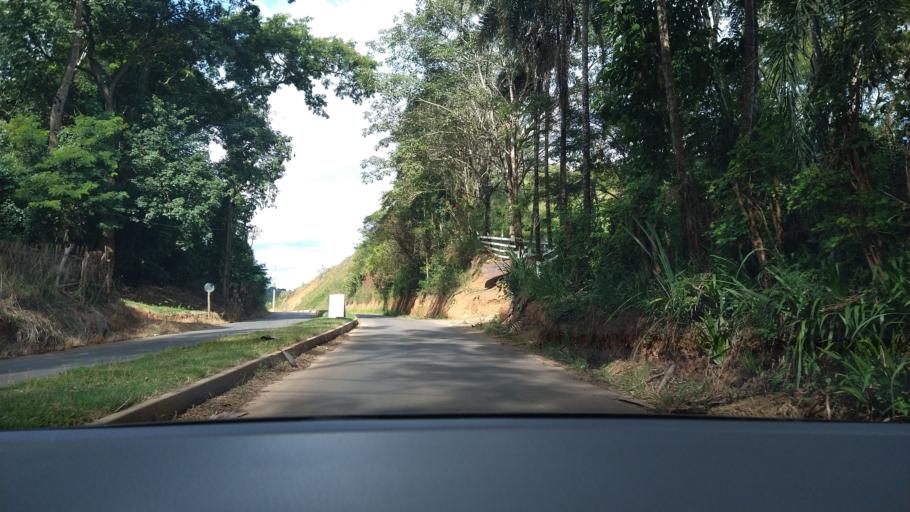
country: BR
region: Minas Gerais
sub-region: Vicosa
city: Vicosa
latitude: -20.7811
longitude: -42.8505
